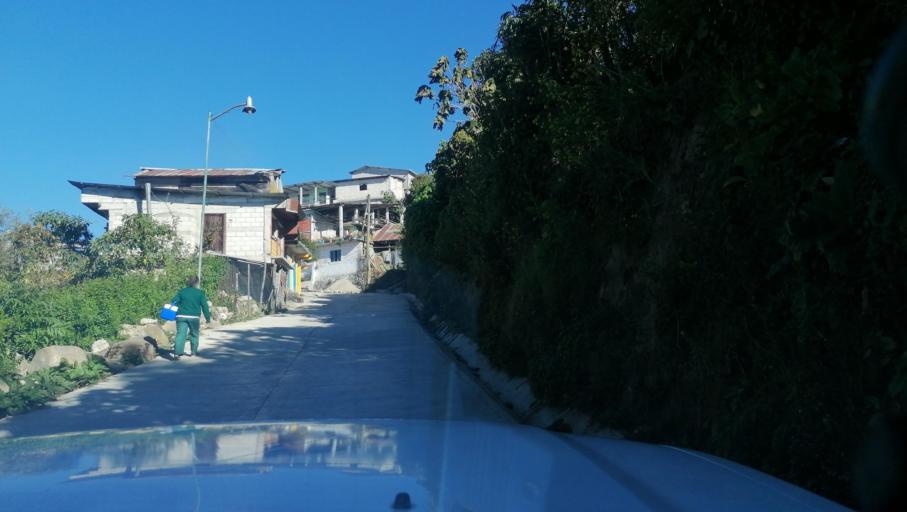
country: MX
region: Chiapas
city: Motozintla de Mendoza
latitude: 15.2585
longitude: -92.2127
